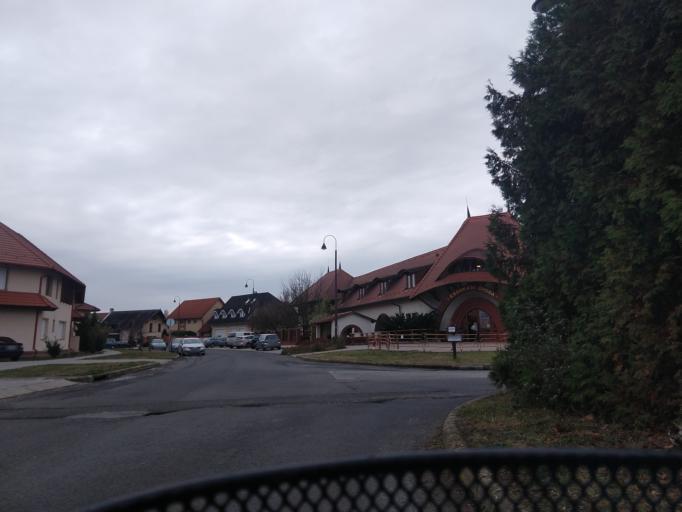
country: HU
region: Pest
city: Veresegyhaz
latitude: 47.6525
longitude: 19.2639
